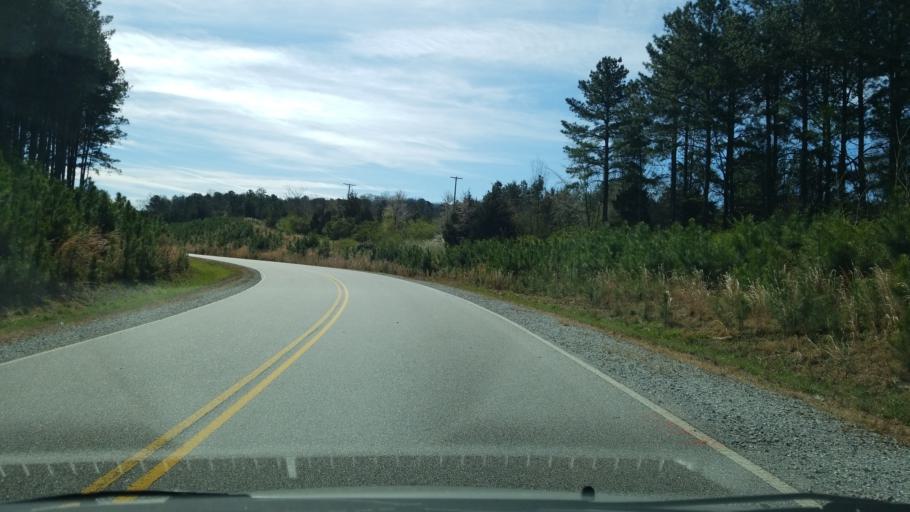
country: US
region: Tennessee
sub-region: Hamilton County
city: Harrison
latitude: 35.1066
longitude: -85.1444
